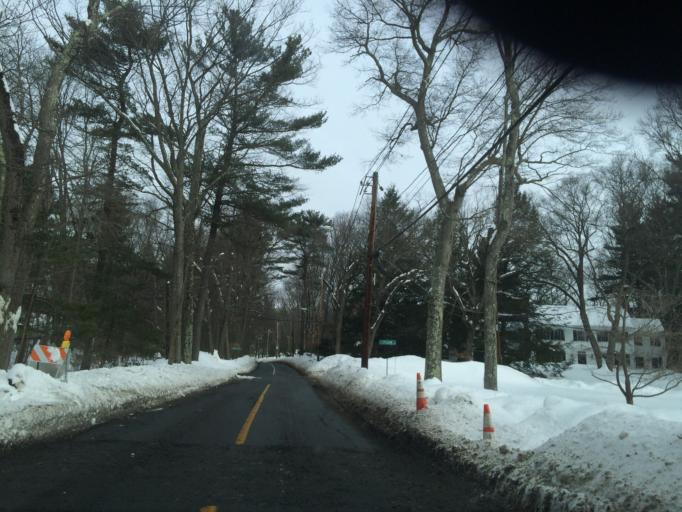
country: US
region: Massachusetts
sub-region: Middlesex County
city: Weston
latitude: 42.3453
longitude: -71.3205
